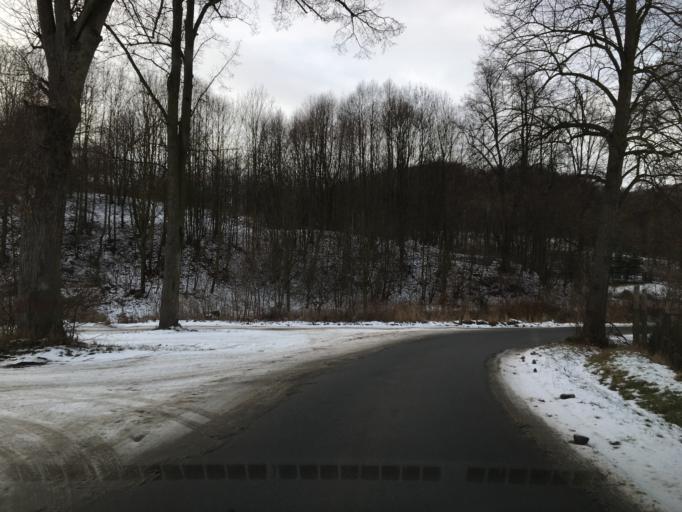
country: PL
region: Lower Silesian Voivodeship
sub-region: Powiat walbrzyski
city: Walim
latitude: 50.7596
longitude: 16.4314
